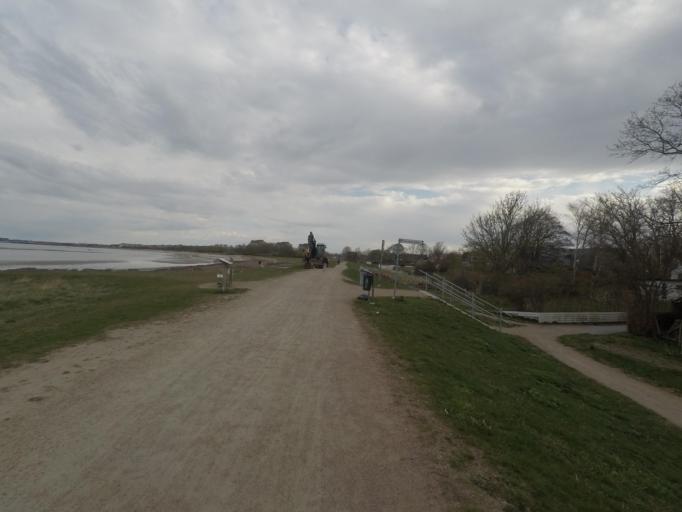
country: SE
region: Skane
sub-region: Lomma Kommun
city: Lomma
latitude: 55.6649
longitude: 13.0625
